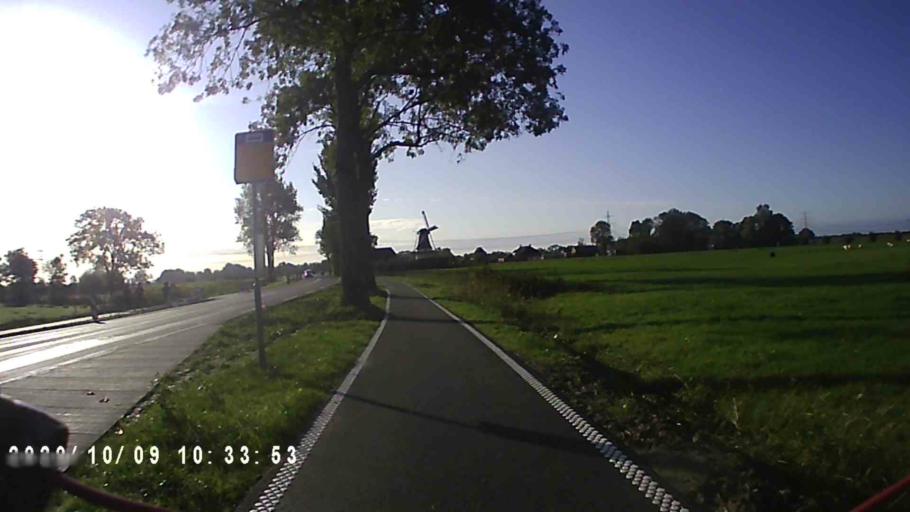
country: NL
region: Groningen
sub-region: Gemeente Winsum
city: Winsum
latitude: 53.3034
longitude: 6.5318
